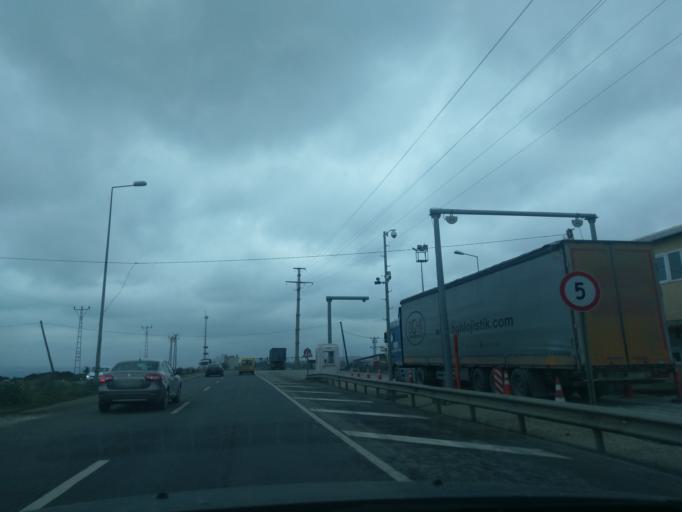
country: TR
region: Istanbul
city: Muratbey
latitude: 41.0967
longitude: 28.5112
